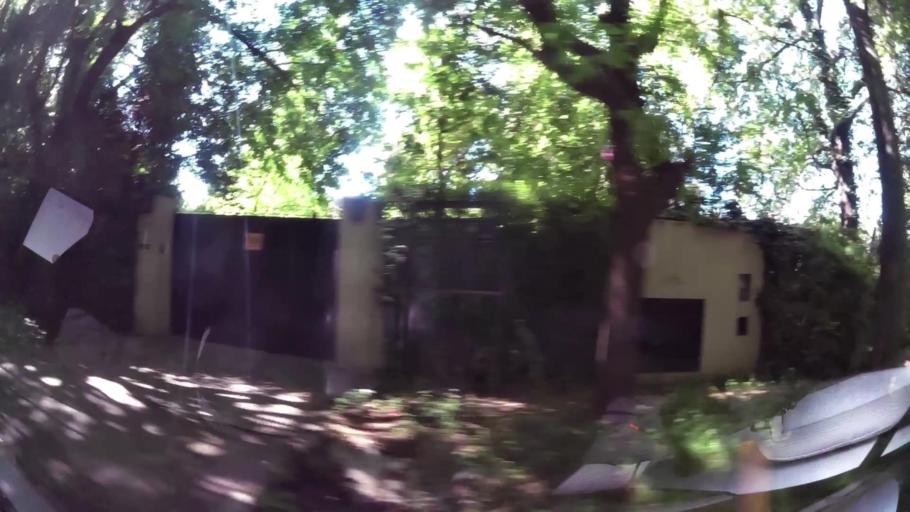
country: AR
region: Buenos Aires
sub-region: Partido de Tigre
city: Tigre
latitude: -34.4952
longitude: -58.6203
